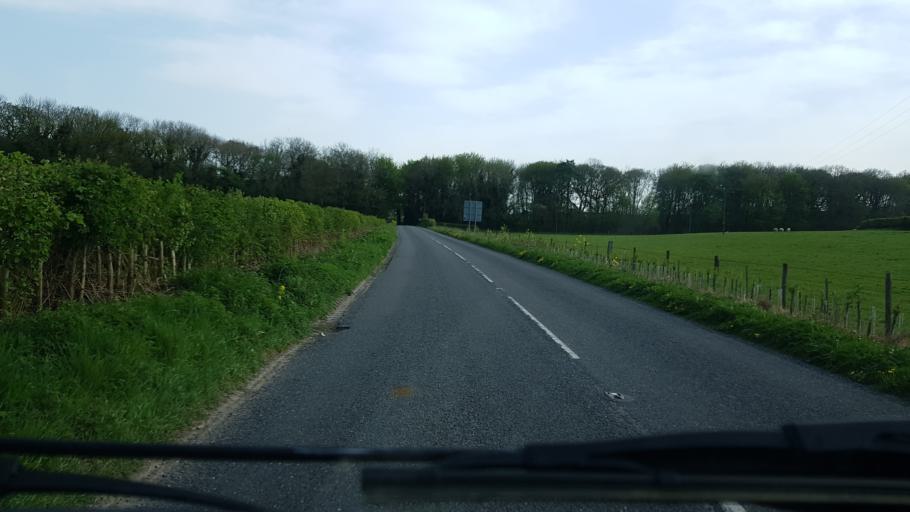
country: GB
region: England
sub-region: Hampshire
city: Kingsclere
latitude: 51.2935
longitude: -1.2665
